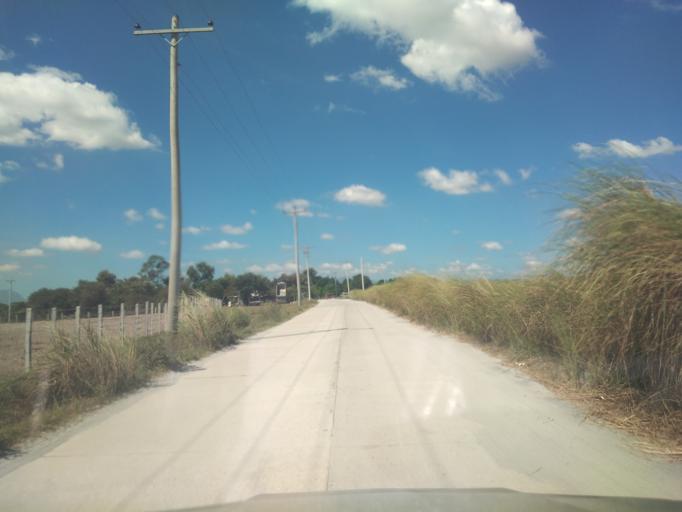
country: PH
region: Central Luzon
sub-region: Province of Pampanga
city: Balas
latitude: 15.0608
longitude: 120.5930
